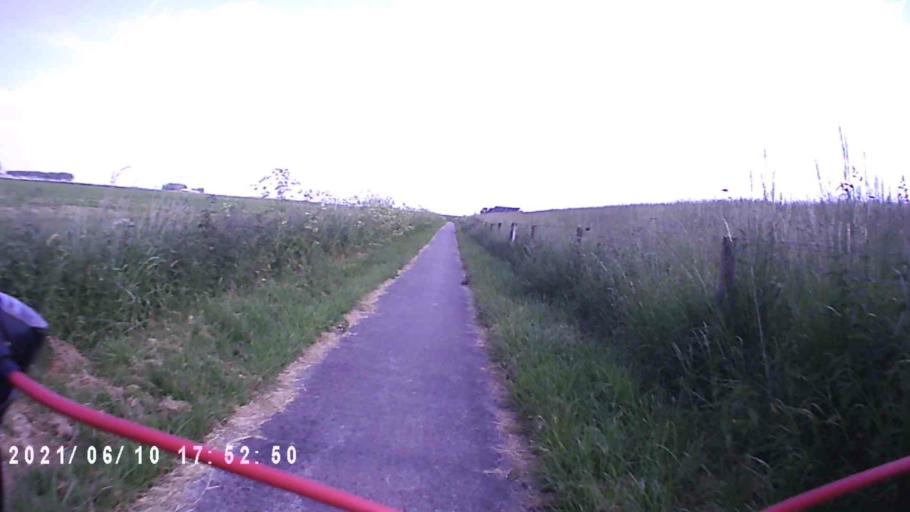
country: NL
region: Groningen
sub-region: Gemeente De Marne
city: Ulrum
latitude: 53.3274
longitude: 6.3198
